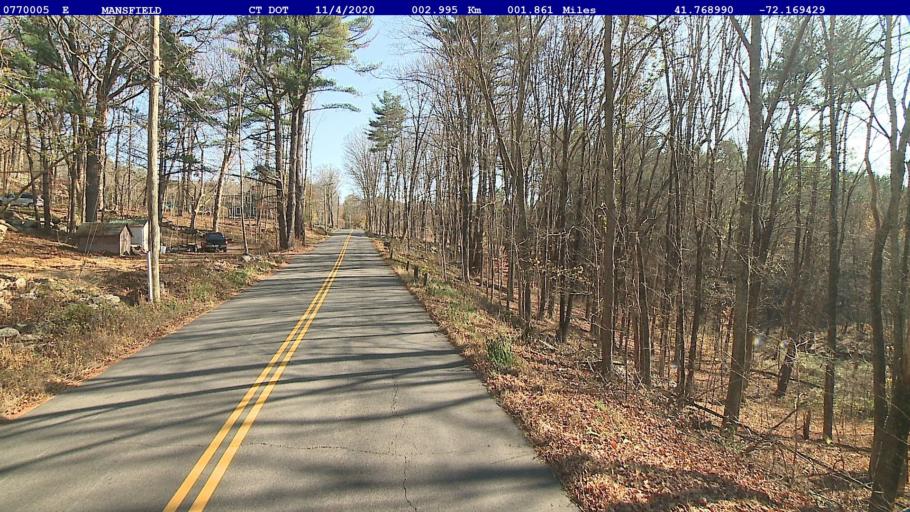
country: US
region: Connecticut
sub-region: Tolland County
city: Mansfield City
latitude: 41.7690
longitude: -72.1694
